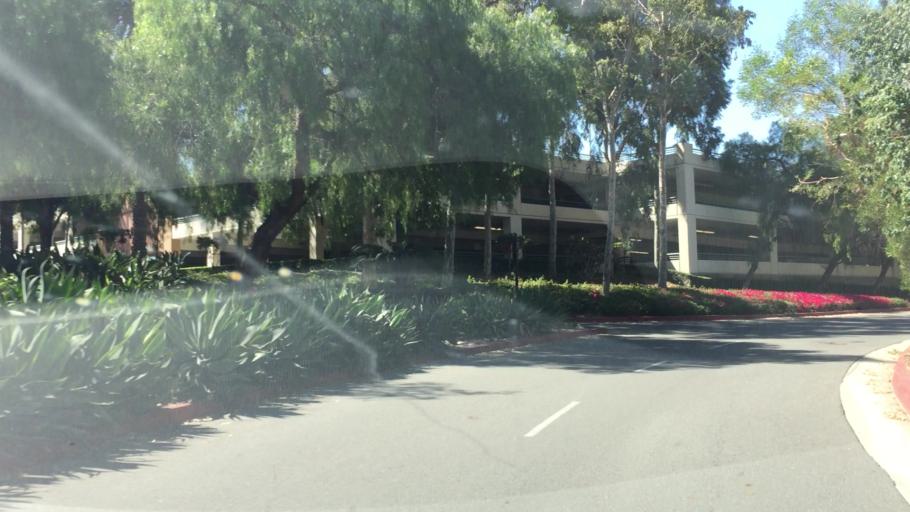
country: US
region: California
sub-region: Orange County
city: Ladera Ranch
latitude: 33.5612
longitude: -117.6692
